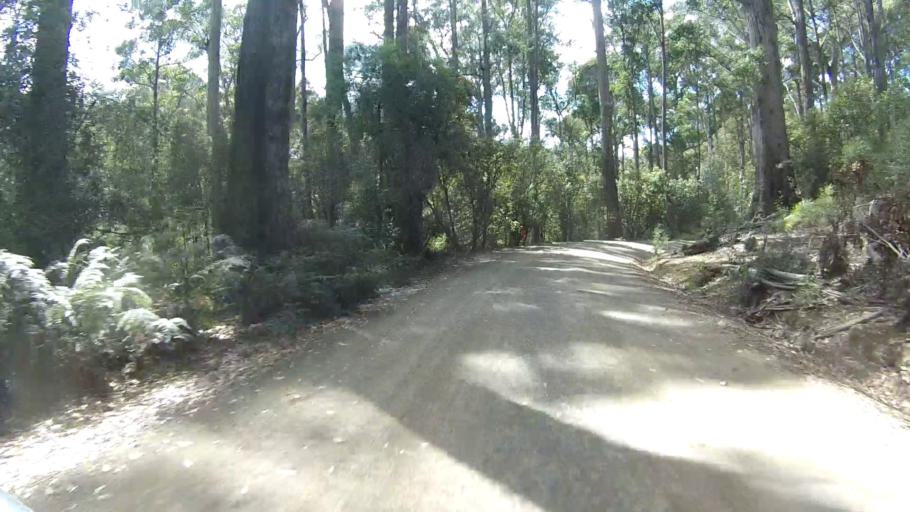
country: AU
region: Tasmania
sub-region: Derwent Valley
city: New Norfolk
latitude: -42.6816
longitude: 146.7129
